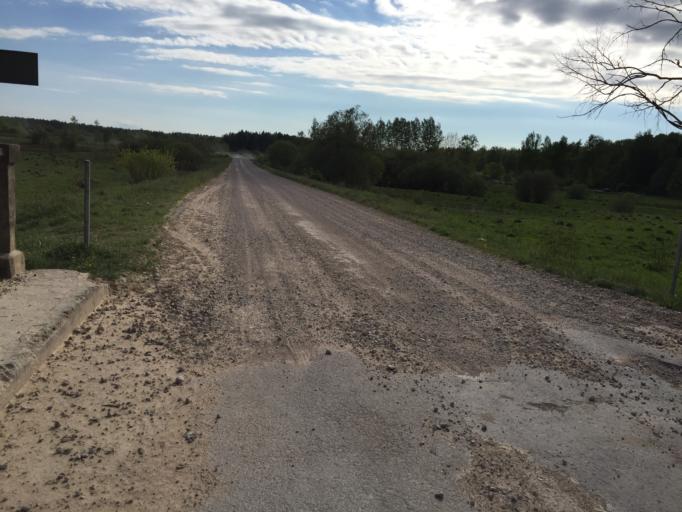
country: LV
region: Lecava
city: Iecava
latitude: 56.6237
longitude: 24.0816
